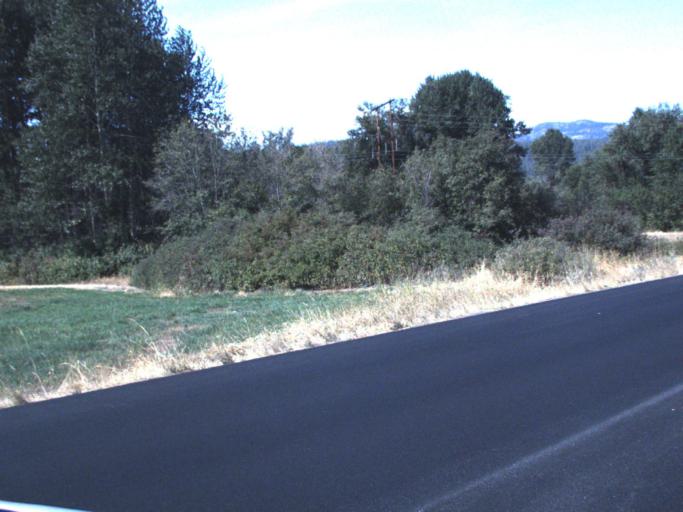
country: US
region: Washington
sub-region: Stevens County
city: Colville
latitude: 48.4761
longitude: -117.8953
